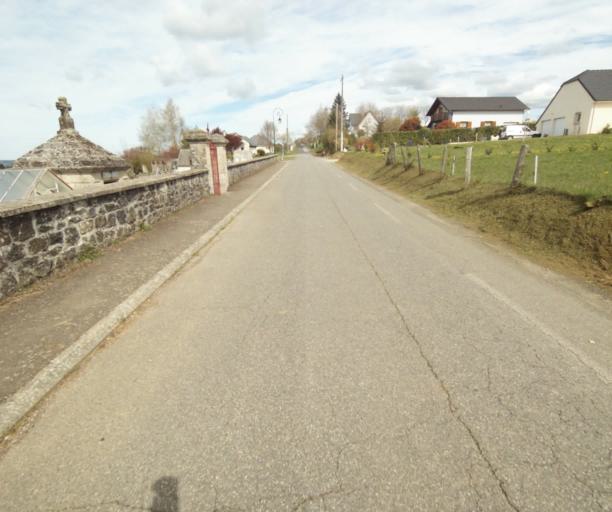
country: FR
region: Limousin
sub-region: Departement de la Correze
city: Laguenne
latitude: 45.2348
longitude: 1.8376
